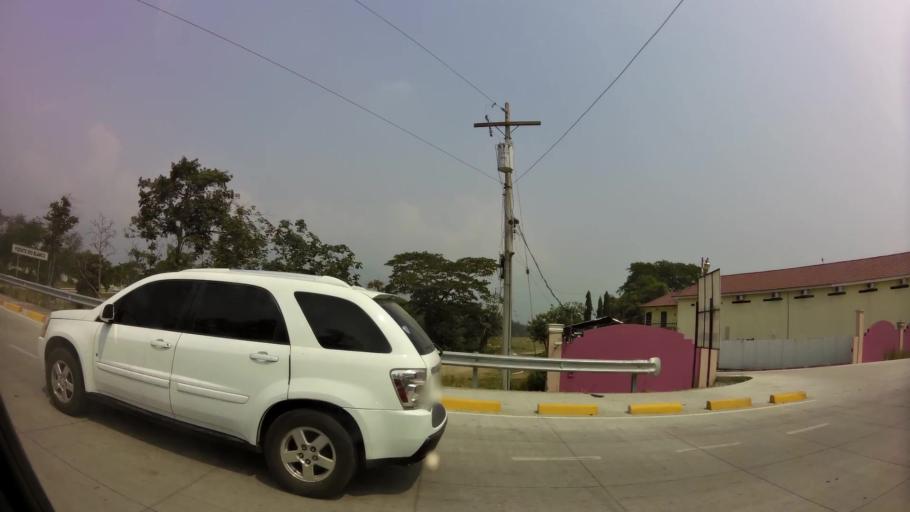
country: HN
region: Cortes
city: San Pedro Sula
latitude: 15.5375
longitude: -88.0020
